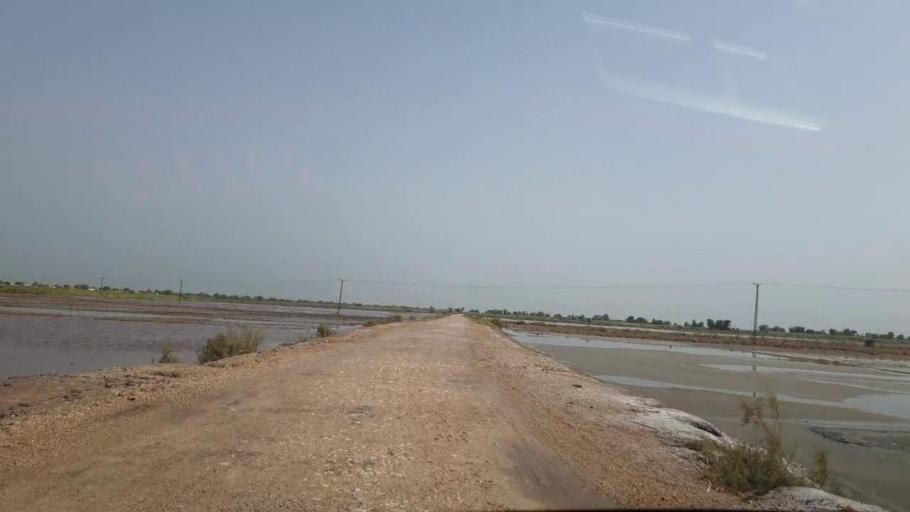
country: PK
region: Sindh
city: Sakrand
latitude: 26.2989
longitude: 68.2202
